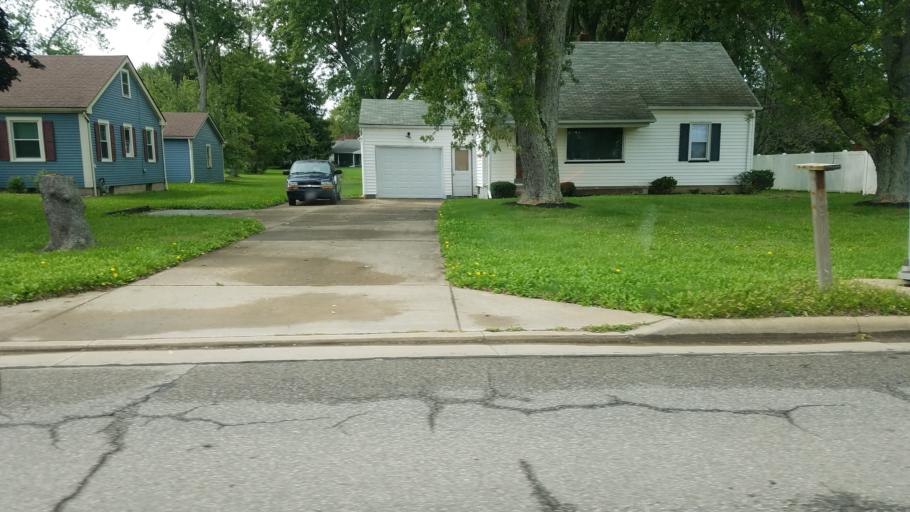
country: US
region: Ohio
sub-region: Mahoning County
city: Poland
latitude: 41.0368
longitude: -80.6348
